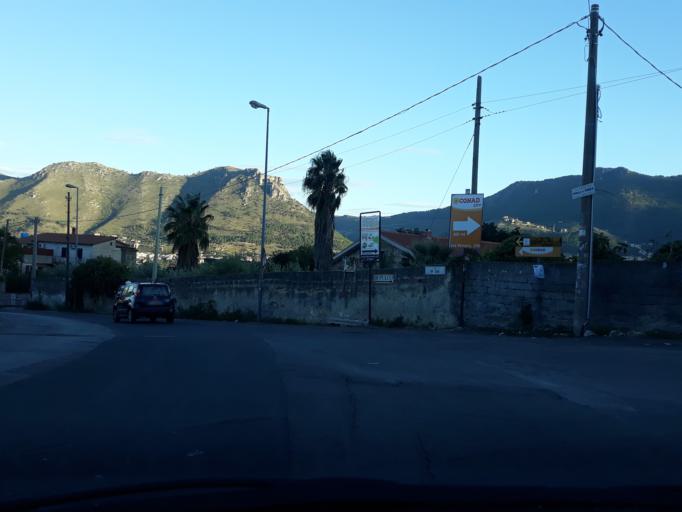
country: IT
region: Sicily
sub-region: Palermo
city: Monreale
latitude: 38.0749
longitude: 13.2886
